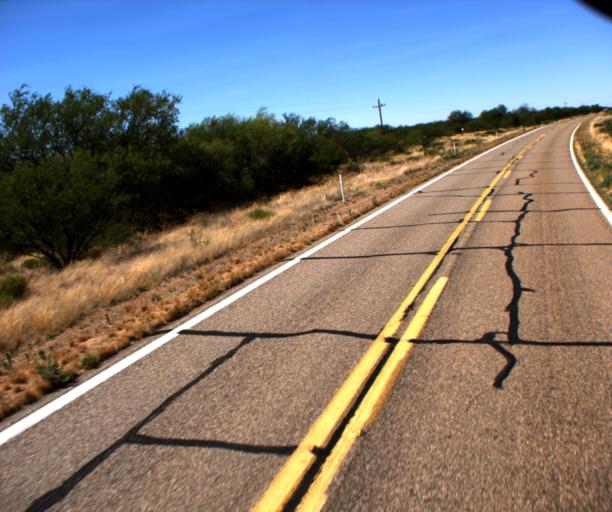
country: US
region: Arizona
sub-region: Pima County
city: Three Points
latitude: 31.7307
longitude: -111.4879
